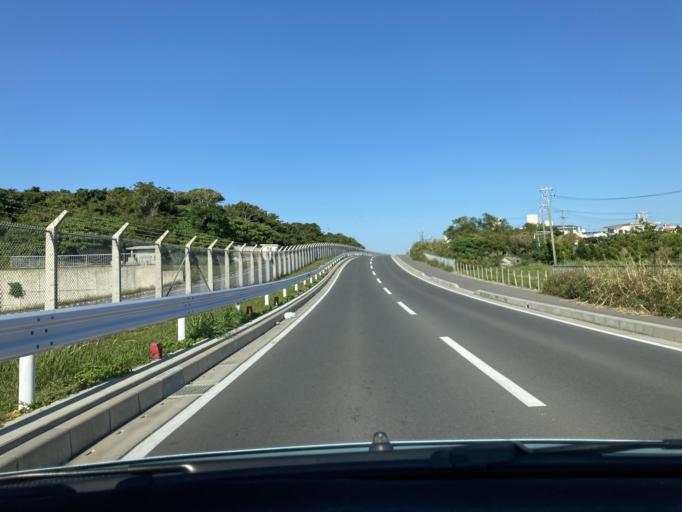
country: JP
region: Okinawa
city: Ginowan
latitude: 26.2686
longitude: 127.7616
